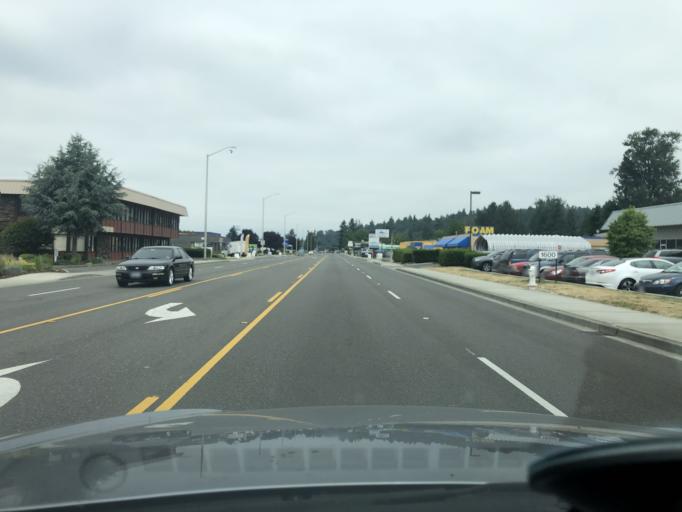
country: US
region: Washington
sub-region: King County
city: Kent
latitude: 47.3649
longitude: -122.2299
